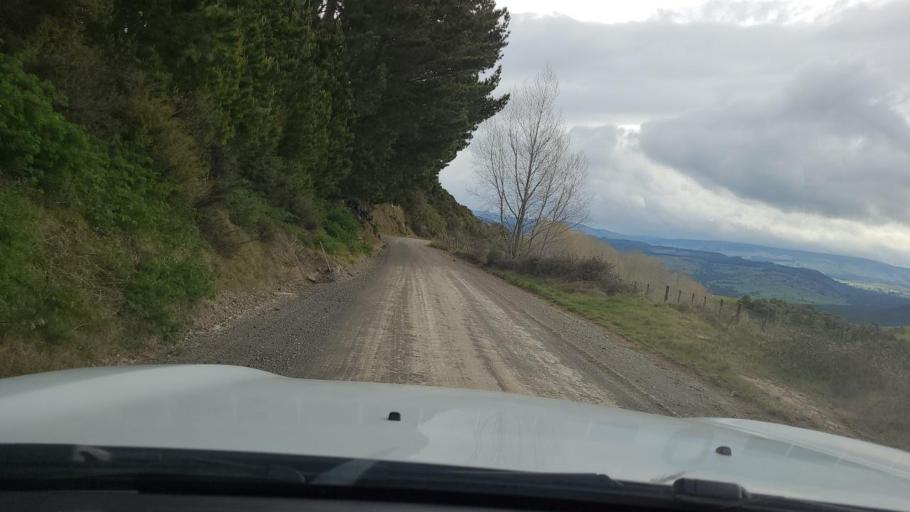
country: NZ
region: Hawke's Bay
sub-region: Napier City
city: Napier
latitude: -39.3073
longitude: 176.8260
